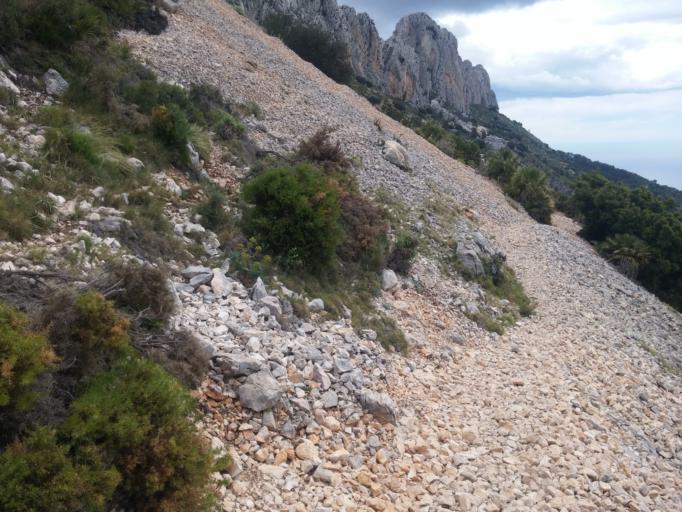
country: ES
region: Valencia
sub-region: Provincia de Alicante
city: Altea
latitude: 38.6591
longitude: -0.0478
